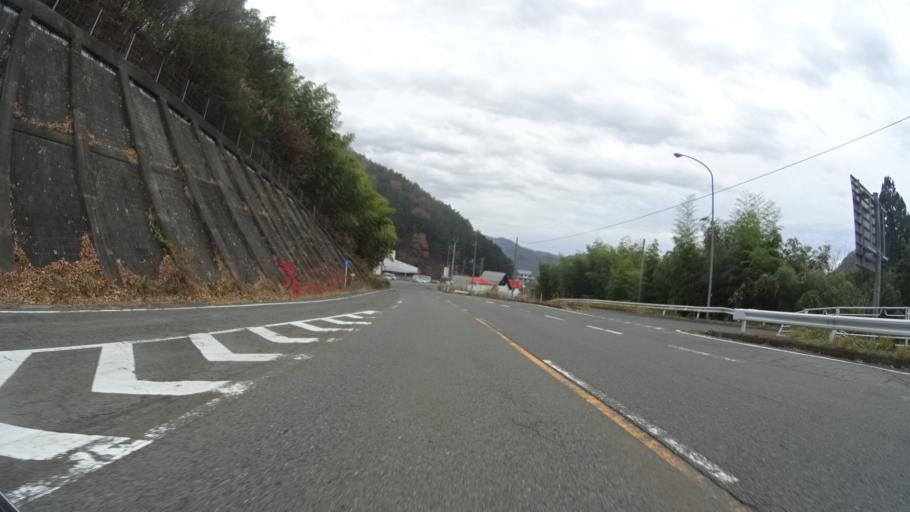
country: JP
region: Gunma
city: Nakanojomachi
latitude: 36.7298
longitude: 138.8776
